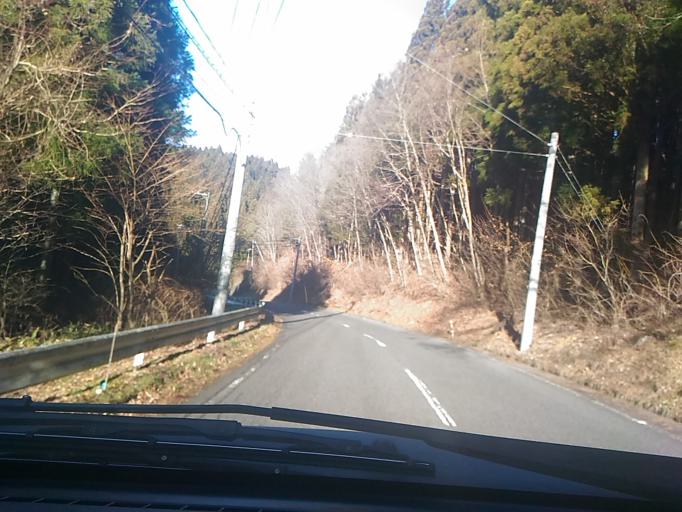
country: JP
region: Fukushima
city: Ishikawa
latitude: 36.9660
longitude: 140.5436
